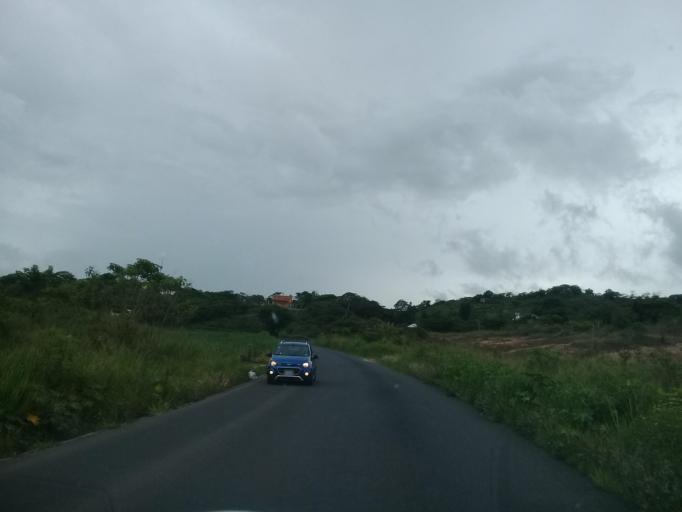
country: MX
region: Veracruz
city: El Castillo
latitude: 19.5617
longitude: -96.8503
